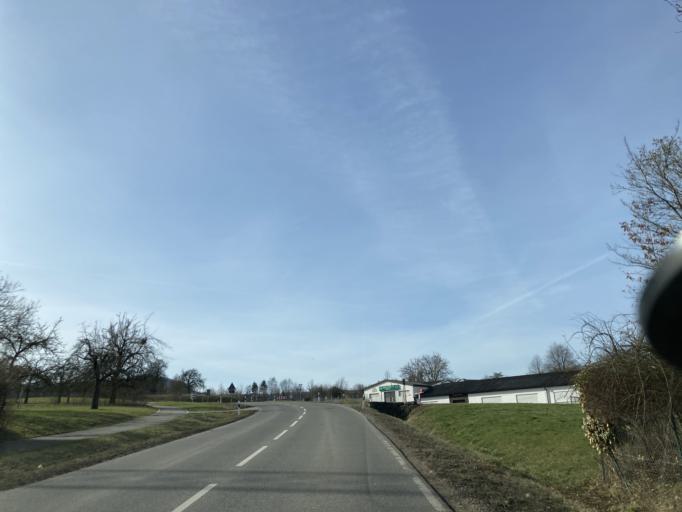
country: DE
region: Baden-Wuerttemberg
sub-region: Tuebingen Region
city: Nehren
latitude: 48.4188
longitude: 9.0666
